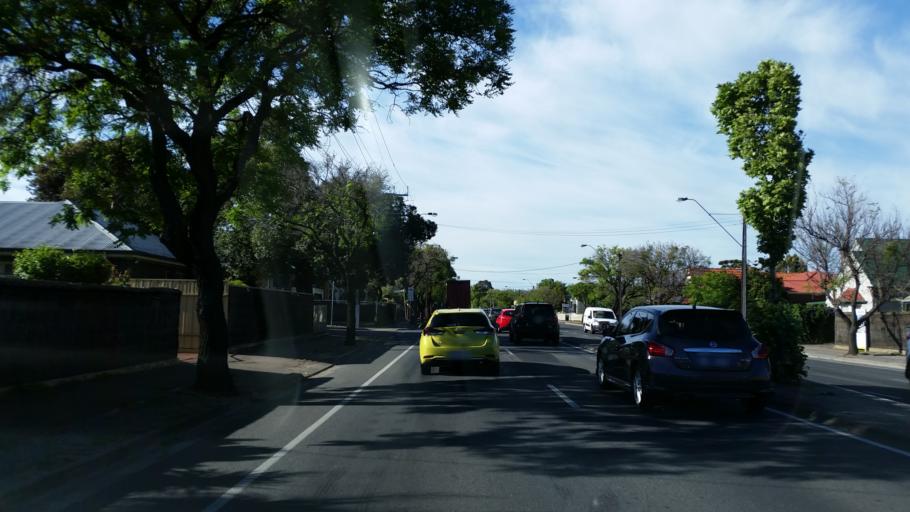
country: AU
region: South Australia
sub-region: Norwood Payneham St Peters
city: Payneham
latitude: -34.8991
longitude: 138.6394
